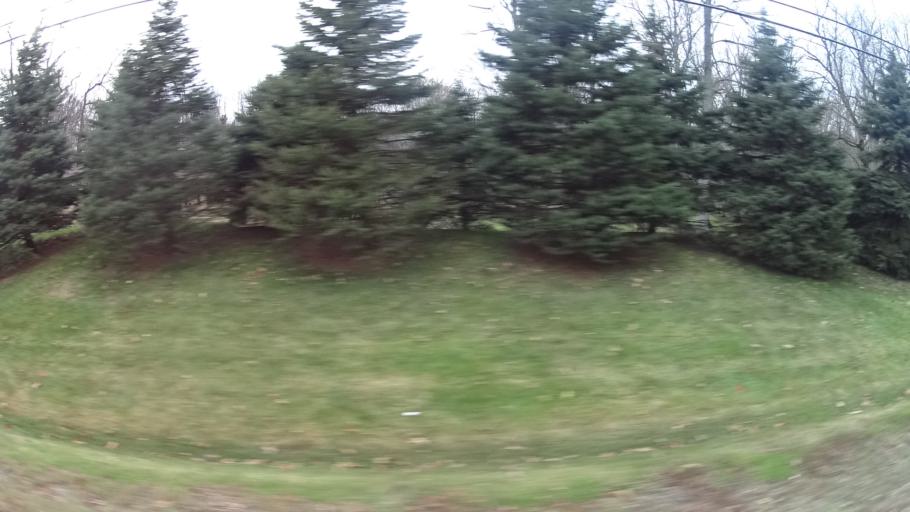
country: US
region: Ohio
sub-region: Lorain County
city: North Ridgeville
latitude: 41.3945
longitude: -82.0584
